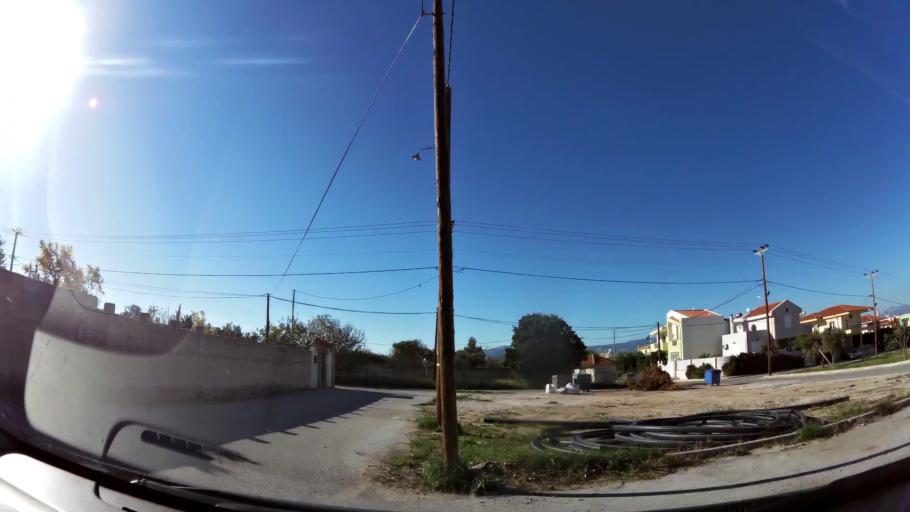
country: GR
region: Attica
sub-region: Nomarchia Anatolikis Attikis
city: Kalyvia Thorikou
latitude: 37.8324
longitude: 23.9290
